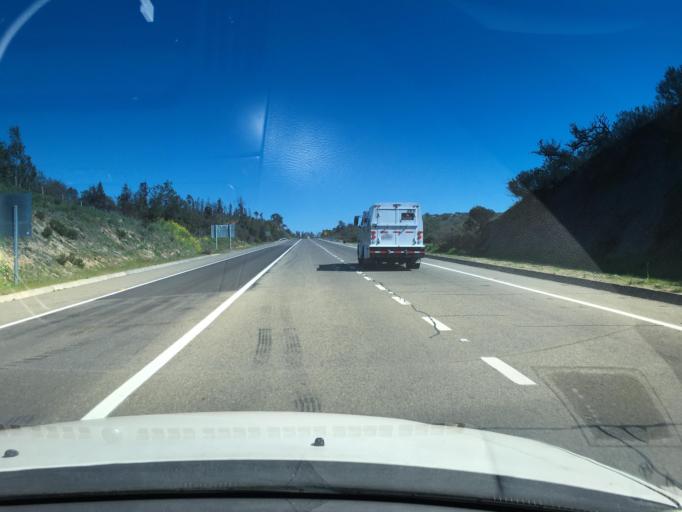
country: CL
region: Valparaiso
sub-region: San Antonio Province
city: El Tabo
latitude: -33.4033
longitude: -71.5013
